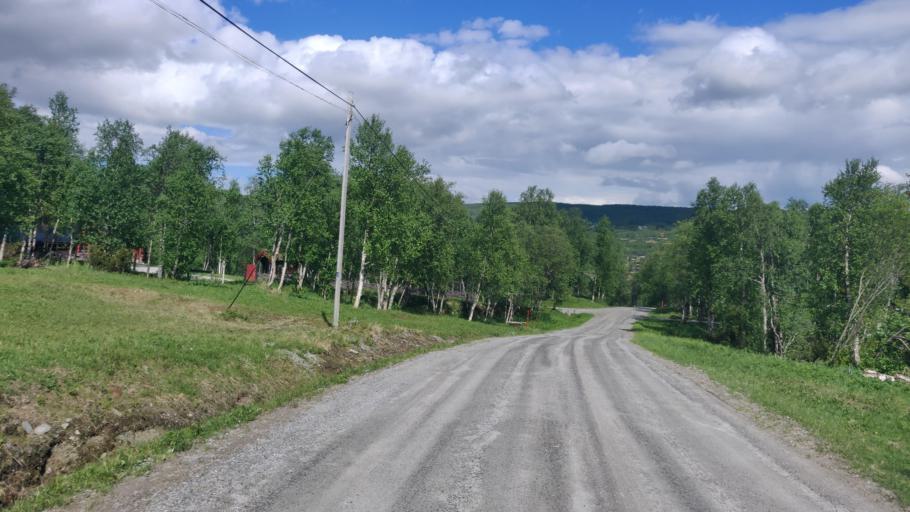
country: NO
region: Sor-Trondelag
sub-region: Tydal
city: Aas
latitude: 62.6416
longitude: 12.4079
